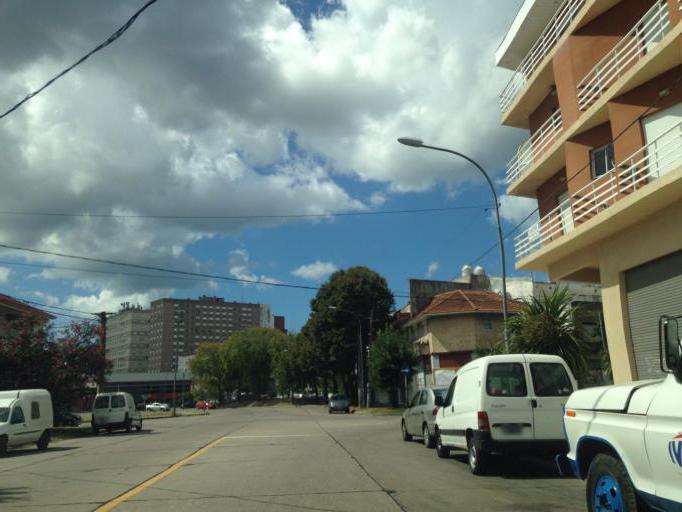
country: AR
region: Buenos Aires
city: Mar del Plata
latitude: -38.0195
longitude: -57.5729
